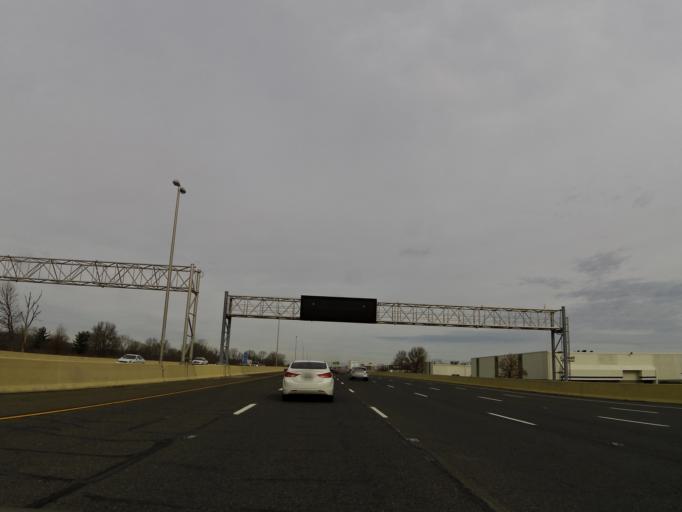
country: US
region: Indiana
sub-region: Boone County
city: Zionsville
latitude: 39.8975
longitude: -86.2696
